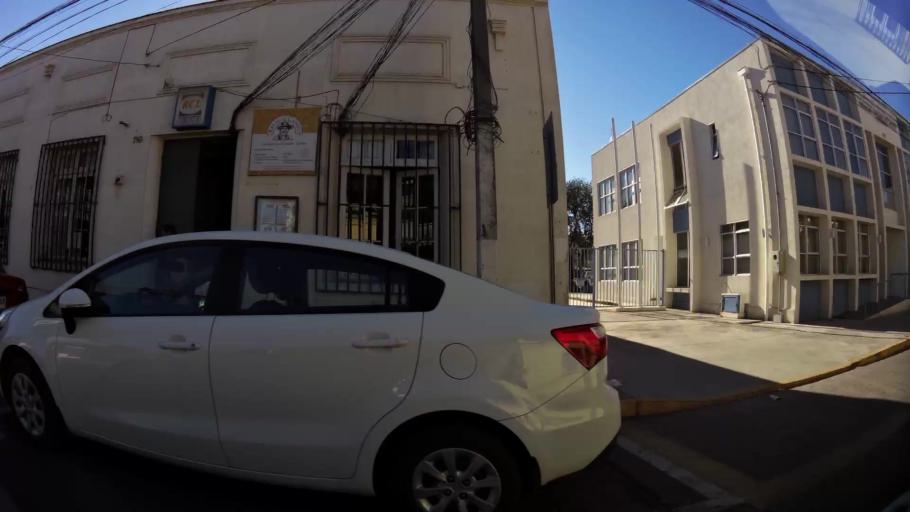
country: CL
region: O'Higgins
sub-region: Provincia de Colchagua
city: Chimbarongo
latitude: -34.5849
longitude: -70.9902
